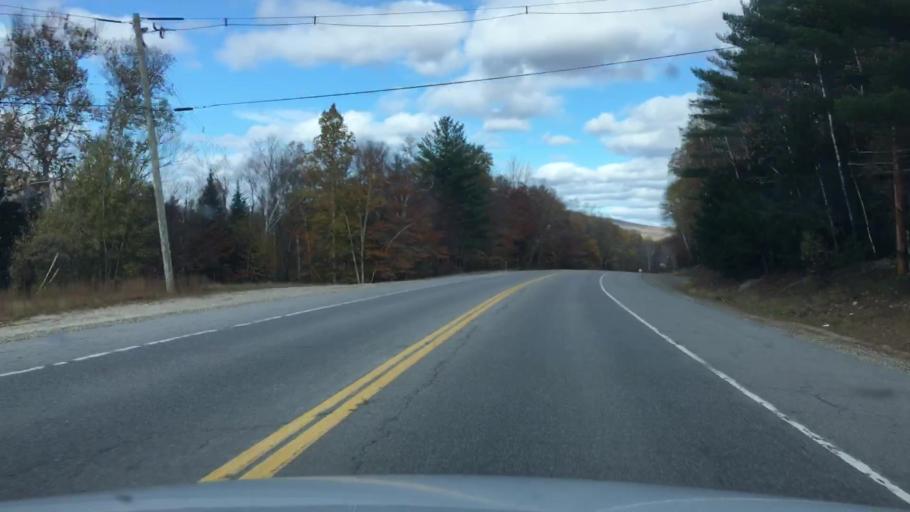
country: US
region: New Hampshire
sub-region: Coos County
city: Gorham
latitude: 44.3226
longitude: -71.2174
